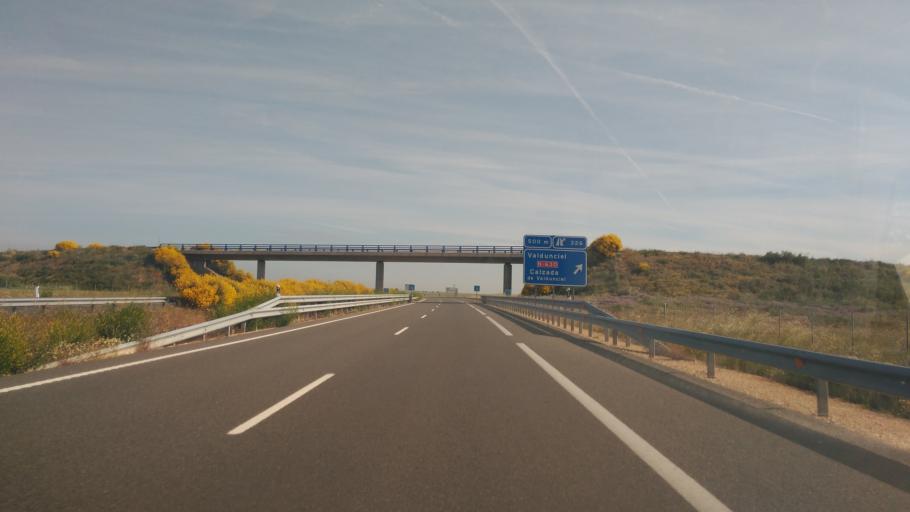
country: ES
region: Castille and Leon
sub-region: Provincia de Salamanca
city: Valdunciel
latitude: 41.0779
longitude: -5.6874
